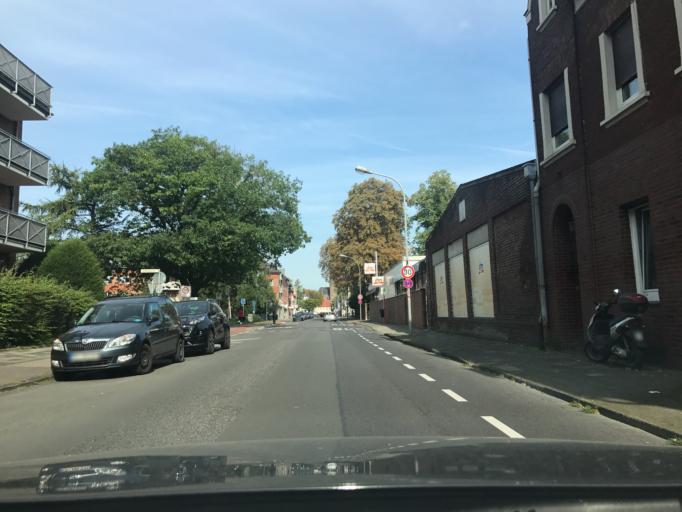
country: DE
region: North Rhine-Westphalia
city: Tonisvorst
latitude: 51.3717
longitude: 6.5034
